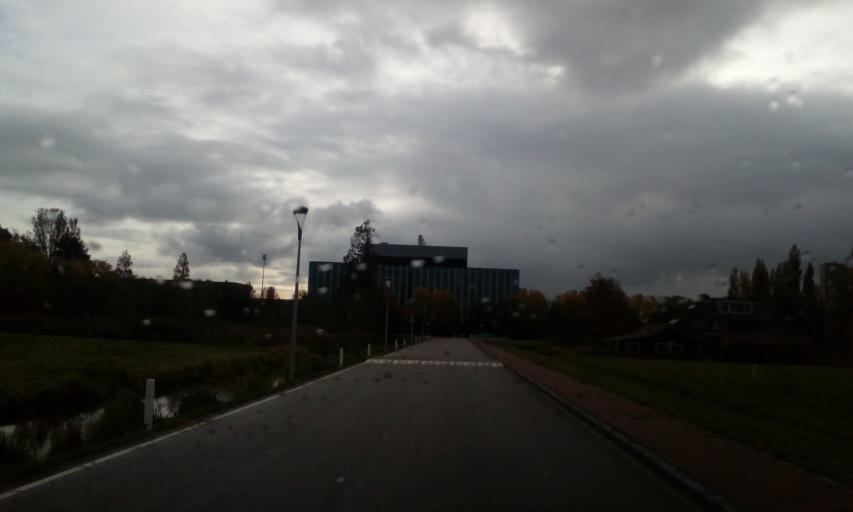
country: NL
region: South Holland
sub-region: Gemeente Rijswijk
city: Rijswijk
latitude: 52.0191
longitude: 4.3365
